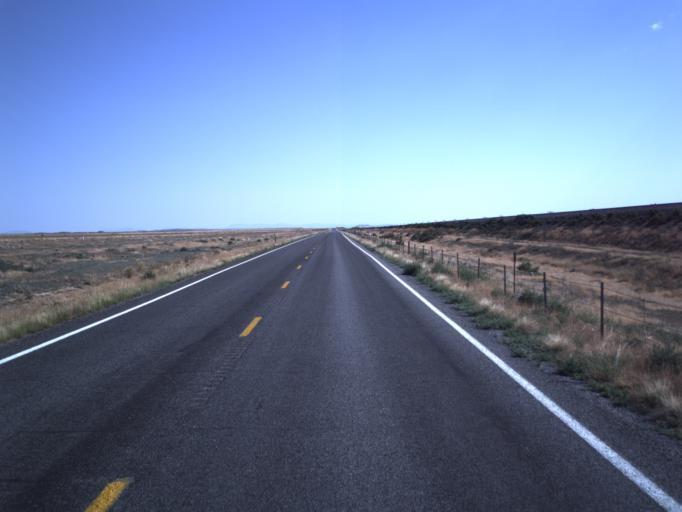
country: US
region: Utah
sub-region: Millard County
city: Delta
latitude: 38.9656
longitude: -112.8012
